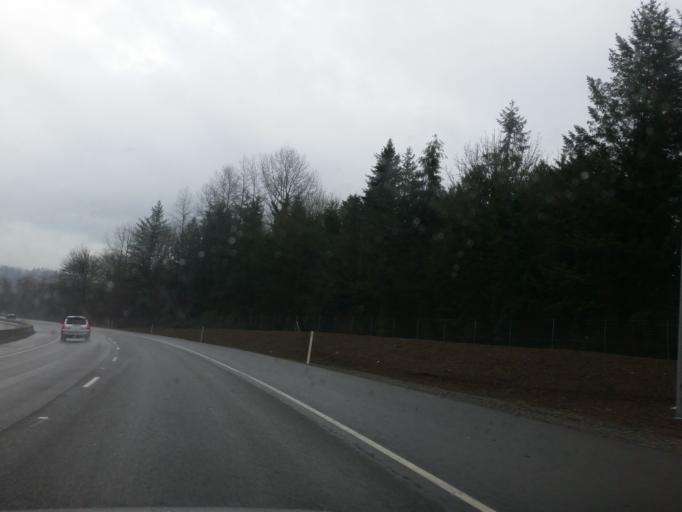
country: US
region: Washington
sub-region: Snohomish County
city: Monroe
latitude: 47.8294
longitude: -122.0319
